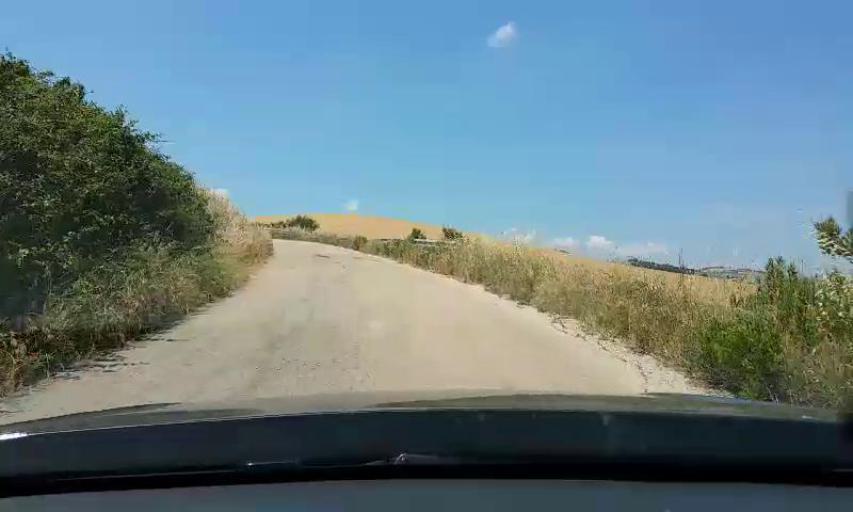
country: IT
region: Molise
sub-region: Provincia di Campobasso
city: Montecilfone
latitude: 41.9223
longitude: 14.8460
